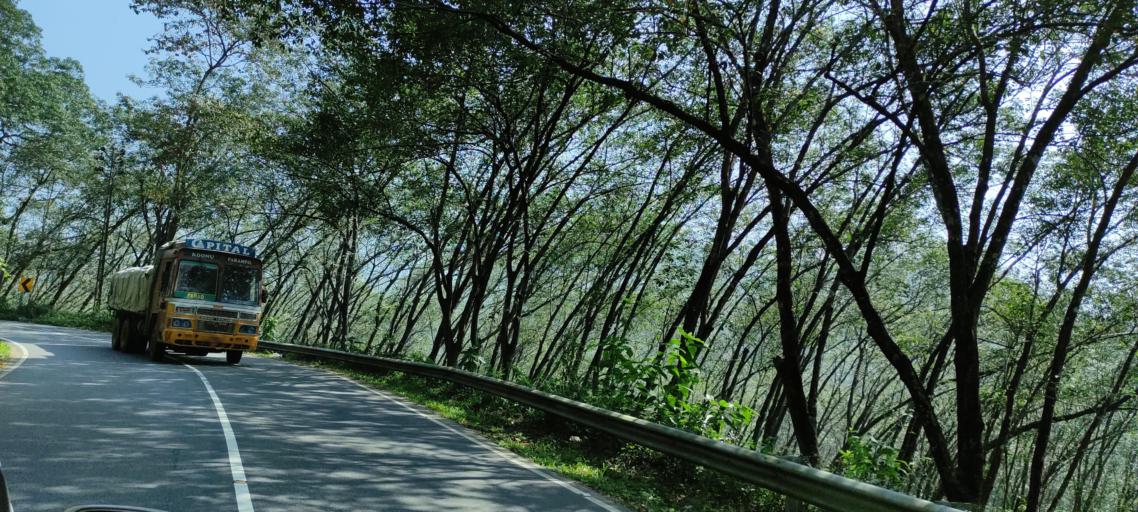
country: IN
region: Kerala
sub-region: Kollam
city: Punalur
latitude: 8.9738
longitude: 77.0620
